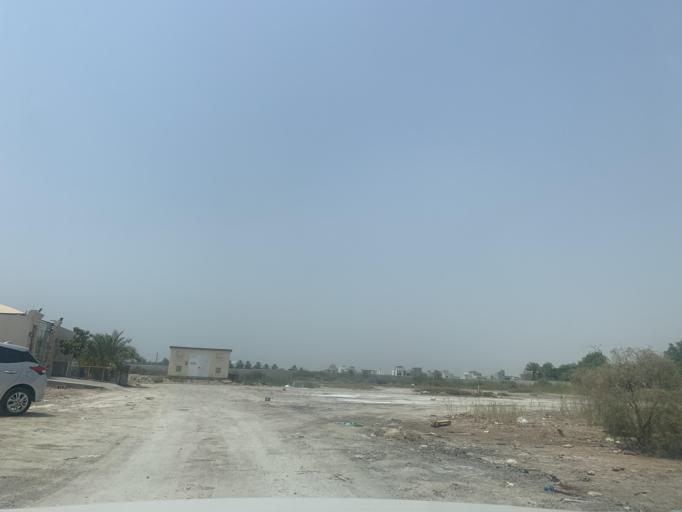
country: BH
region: Central Governorate
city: Madinat Hamad
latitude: 26.1249
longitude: 50.4655
